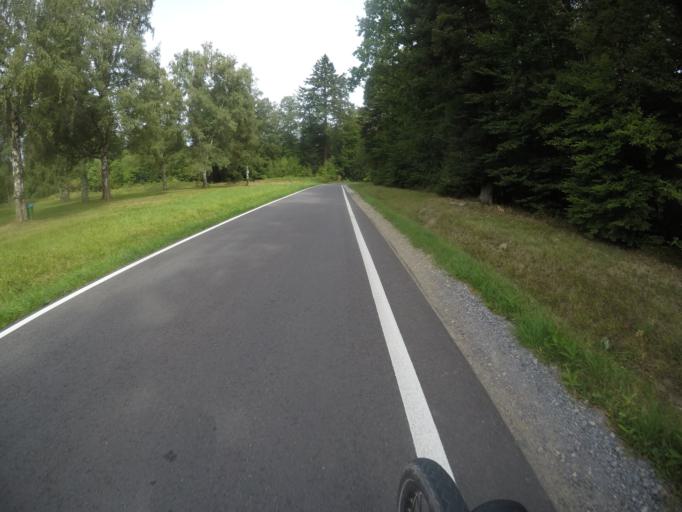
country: DE
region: Baden-Wuerttemberg
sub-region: Karlsruhe Region
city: Eutingen
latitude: 48.8721
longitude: 8.7615
